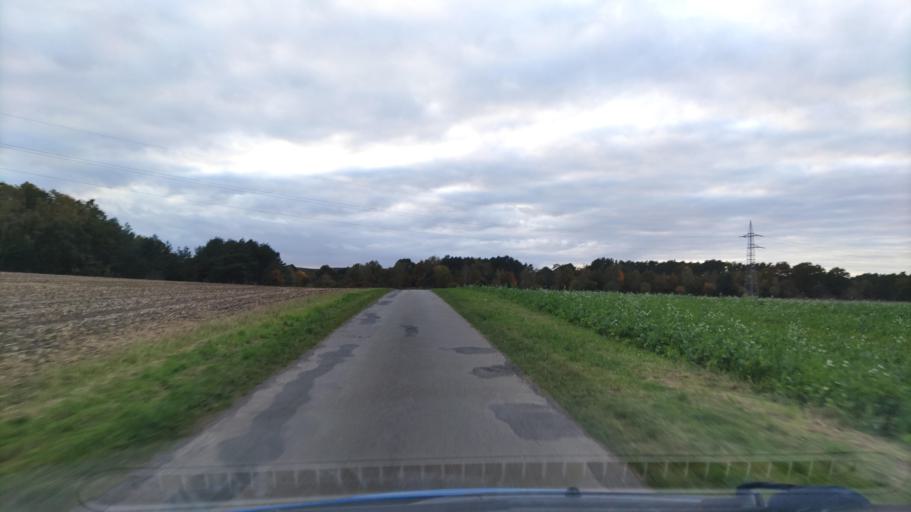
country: DE
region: Lower Saxony
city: Karwitz
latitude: 53.1303
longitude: 10.9728
